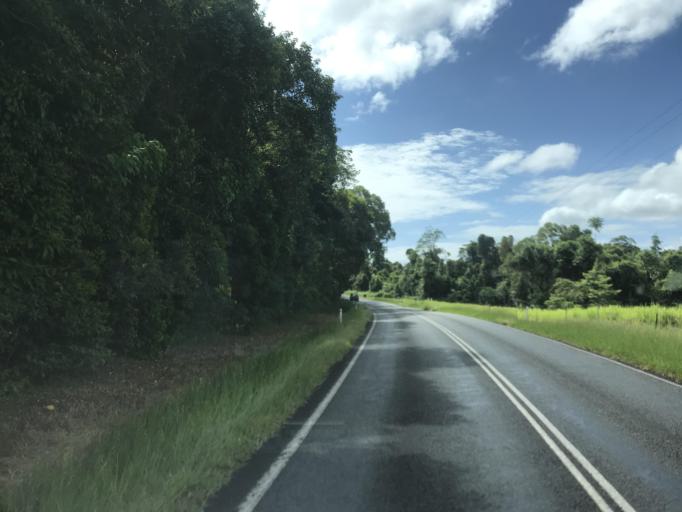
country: AU
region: Queensland
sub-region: Cassowary Coast
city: Innisfail
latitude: -17.8478
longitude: 146.0582
